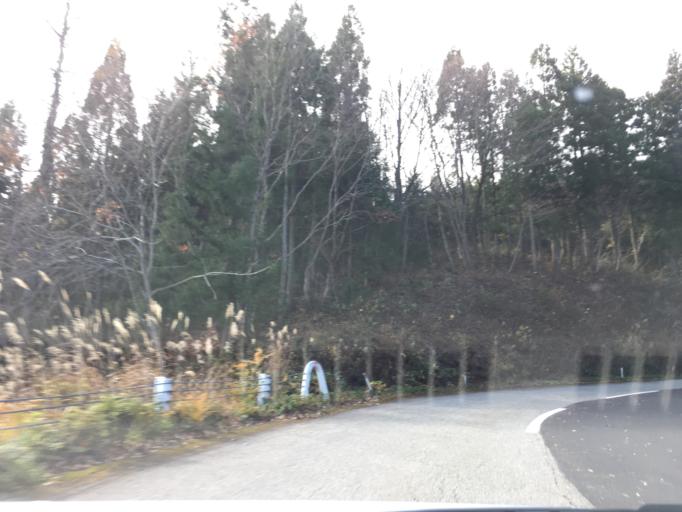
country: JP
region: Fukushima
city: Inawashiro
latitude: 37.4576
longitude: 140.0025
